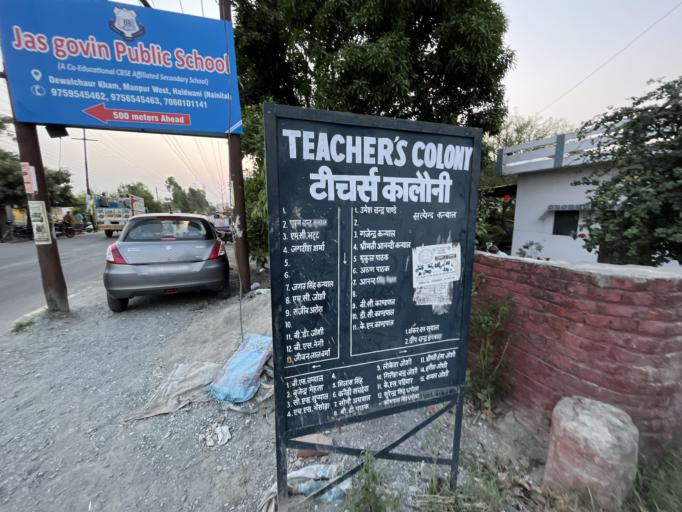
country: IN
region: Uttarakhand
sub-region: Naini Tal
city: Haldwani
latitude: 29.1944
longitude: 79.5025
